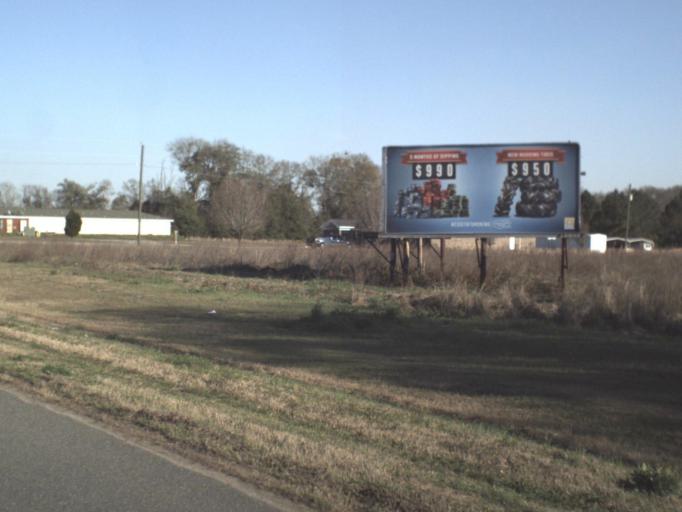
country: US
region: Florida
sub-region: Jackson County
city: Sneads
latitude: 30.7084
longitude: -84.9062
